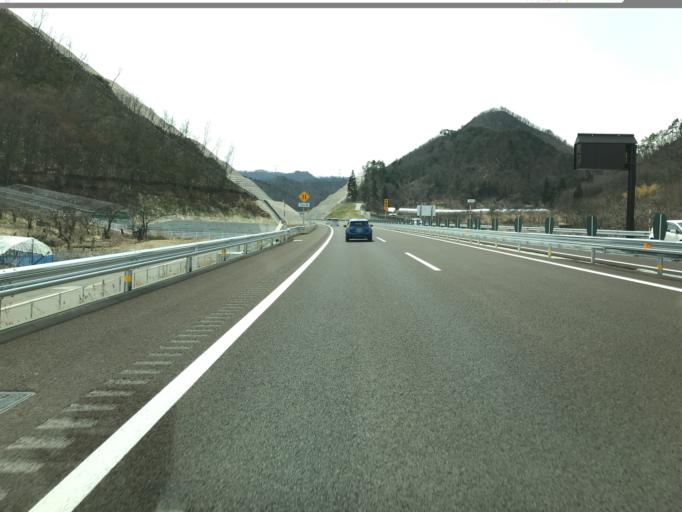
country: JP
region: Yamagata
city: Kaminoyama
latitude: 38.1234
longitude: 140.2522
